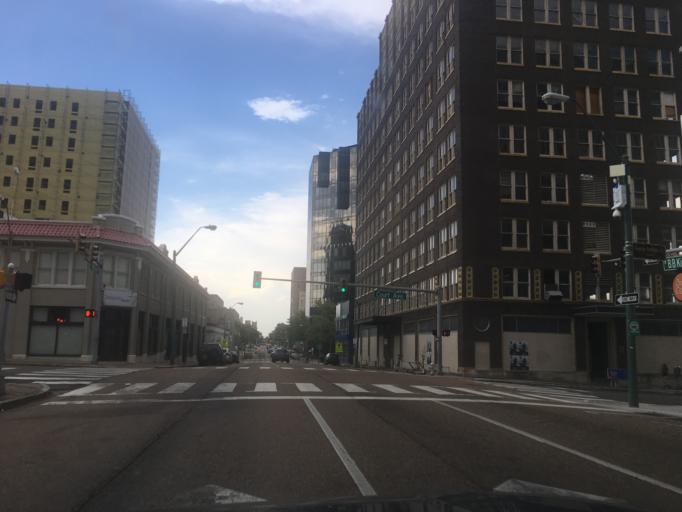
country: US
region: Tennessee
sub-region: Shelby County
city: Memphis
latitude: 35.1452
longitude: -90.0500
